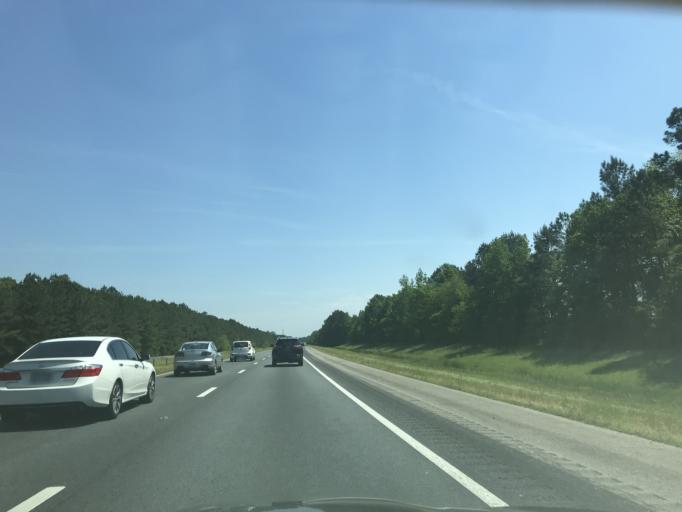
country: US
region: North Carolina
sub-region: Johnston County
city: Benson
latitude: 35.3645
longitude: -78.4908
